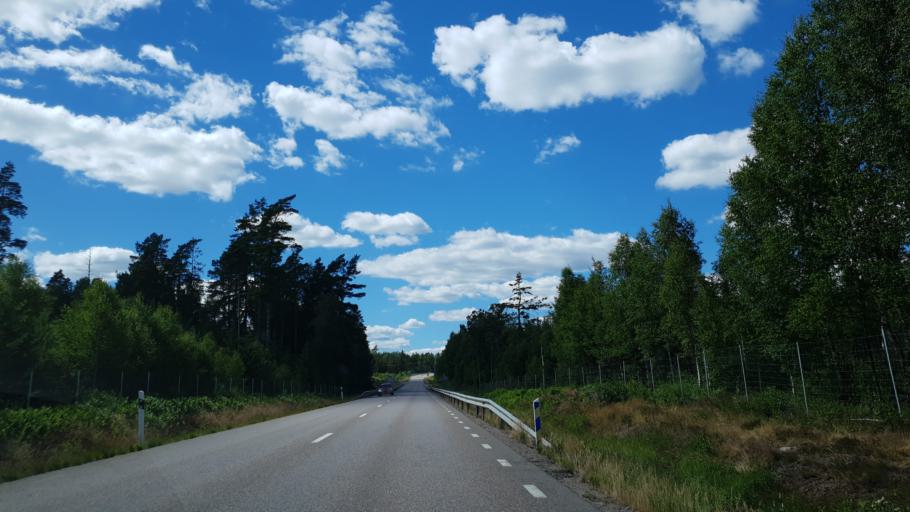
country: SE
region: Kronoberg
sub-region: Lessebo Kommun
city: Hovmantorp
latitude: 56.7915
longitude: 15.1326
